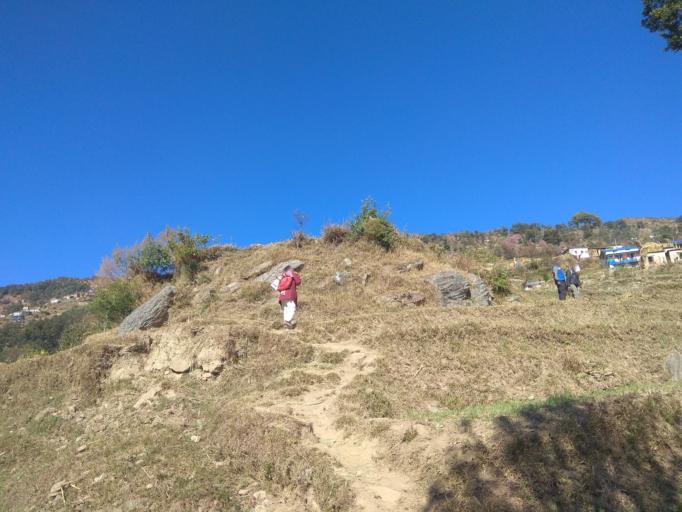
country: NP
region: Far Western
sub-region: Seti Zone
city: Achham
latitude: 29.2553
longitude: 81.6348
